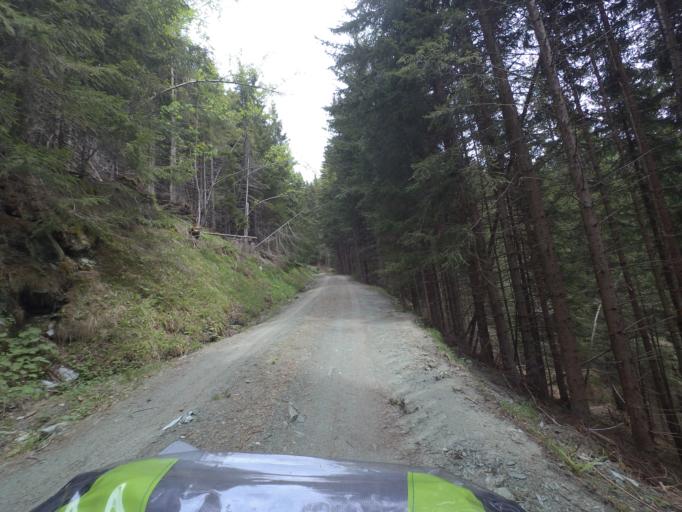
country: AT
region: Salzburg
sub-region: Politischer Bezirk Sankt Johann im Pongau
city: Dorfgastein
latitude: 47.2602
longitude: 13.1242
